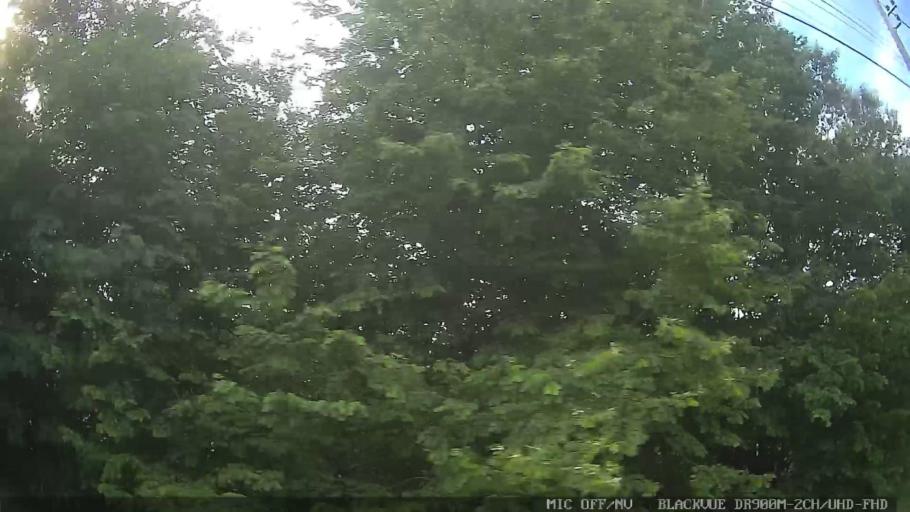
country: BR
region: Minas Gerais
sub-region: Extrema
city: Extrema
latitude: -22.8631
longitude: -46.3340
